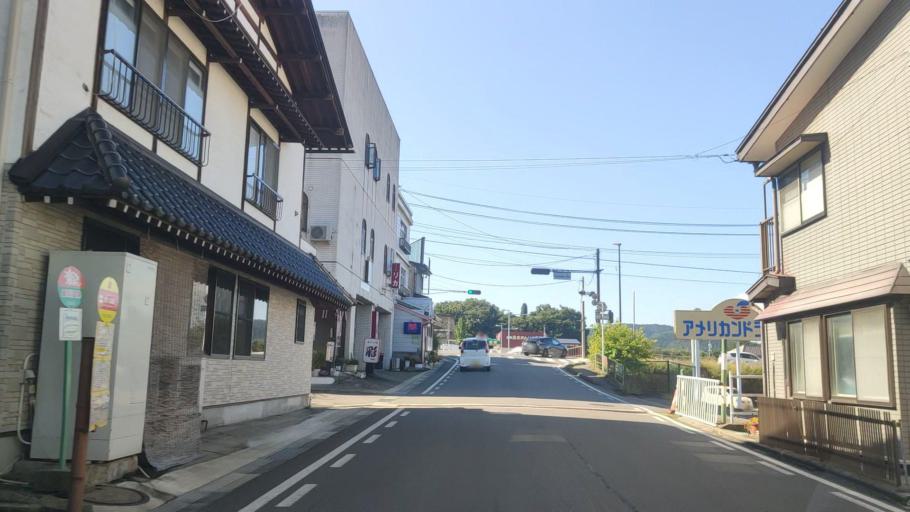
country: JP
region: Nagano
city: Nakano
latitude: 36.7395
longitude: 138.4157
